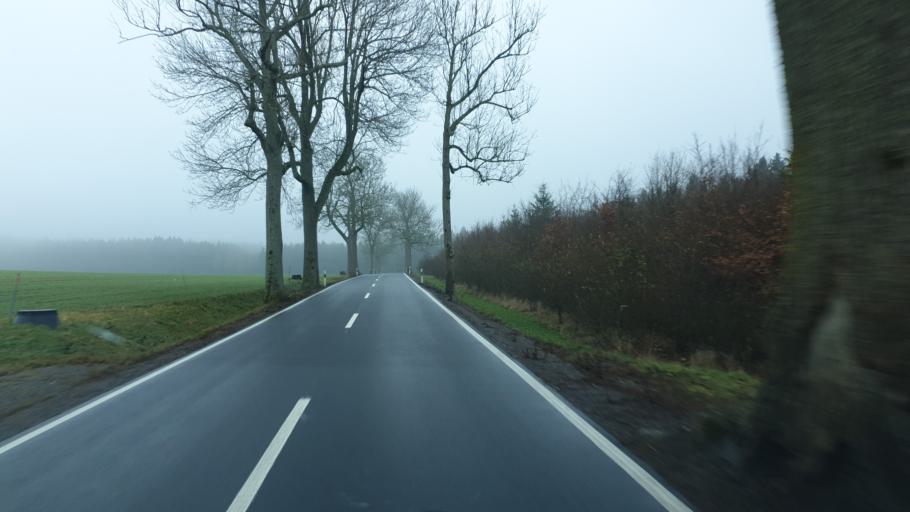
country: DE
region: Saxony
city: Sayda
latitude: 50.7017
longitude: 13.4399
